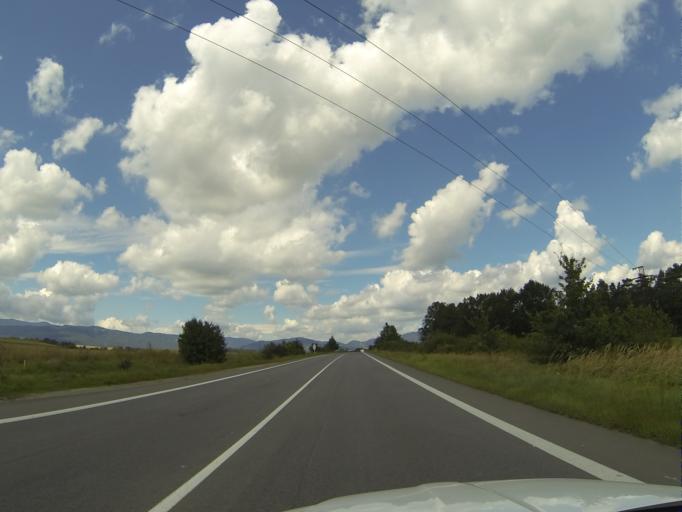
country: SK
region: Banskobystricky
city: Ziar nad Hronom
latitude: 48.6027
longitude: 18.8401
